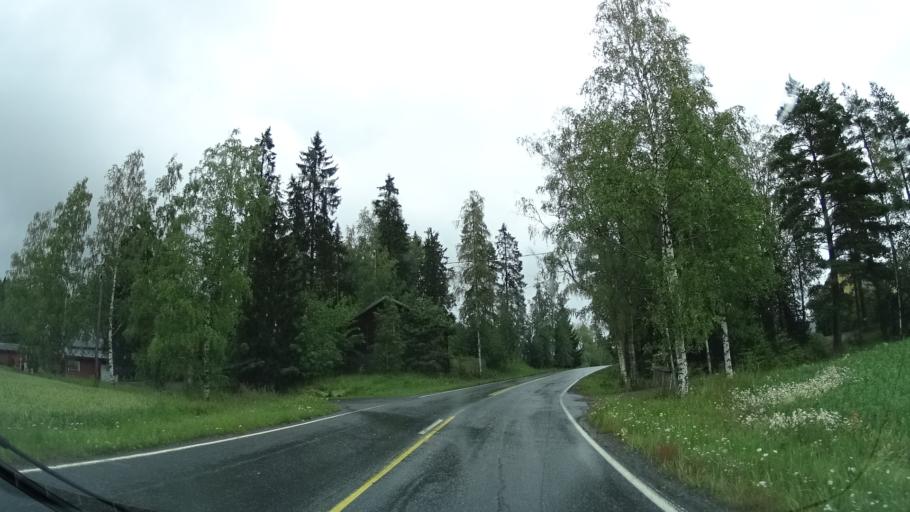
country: FI
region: Haeme
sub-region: Forssa
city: Humppila
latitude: 61.0045
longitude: 23.2522
